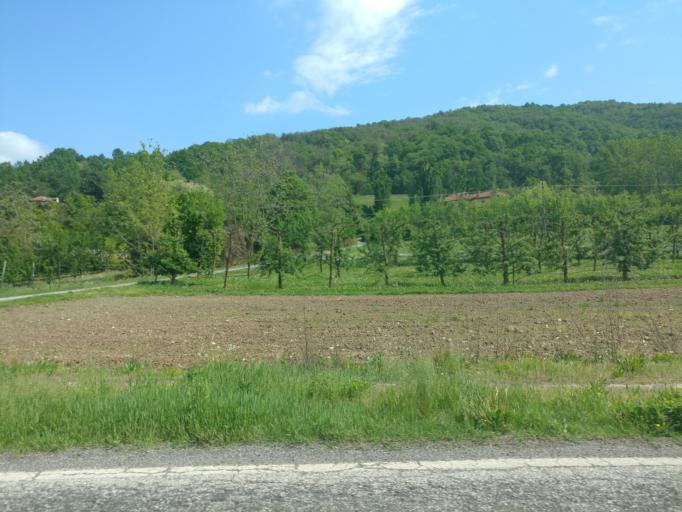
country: IT
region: Piedmont
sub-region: Provincia di Cuneo
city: Castellar
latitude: 44.6251
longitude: 7.4510
